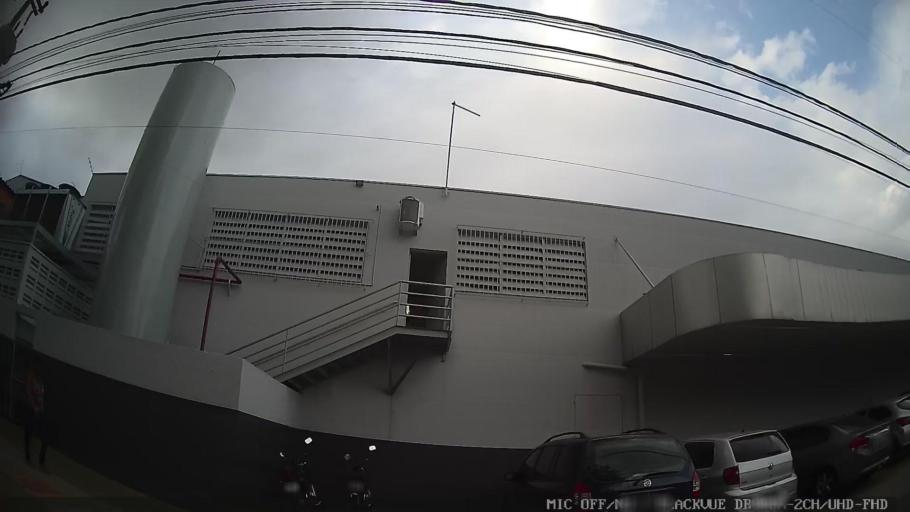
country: BR
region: Sao Paulo
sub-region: Indaiatuba
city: Indaiatuba
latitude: -23.1155
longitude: -47.2413
